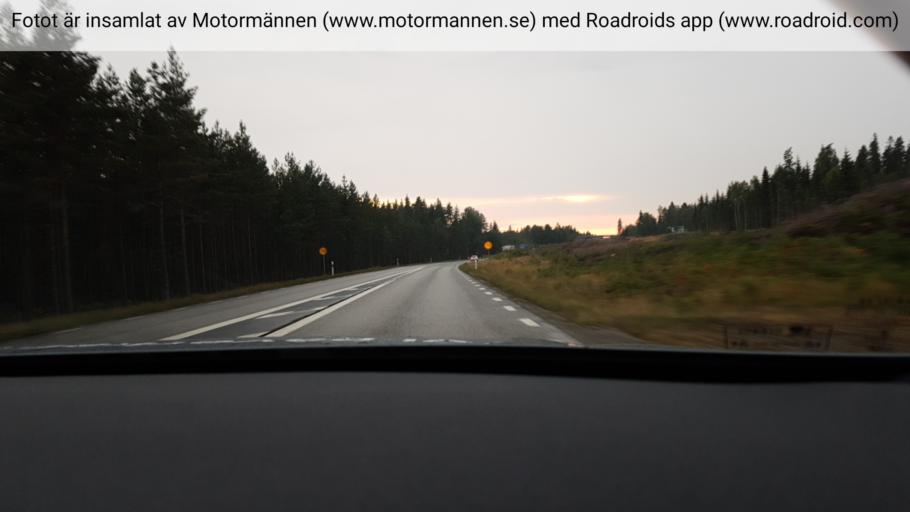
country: SE
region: Joenkoeping
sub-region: Mullsjo Kommun
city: Mullsjoe
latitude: 57.8745
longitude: 13.9300
